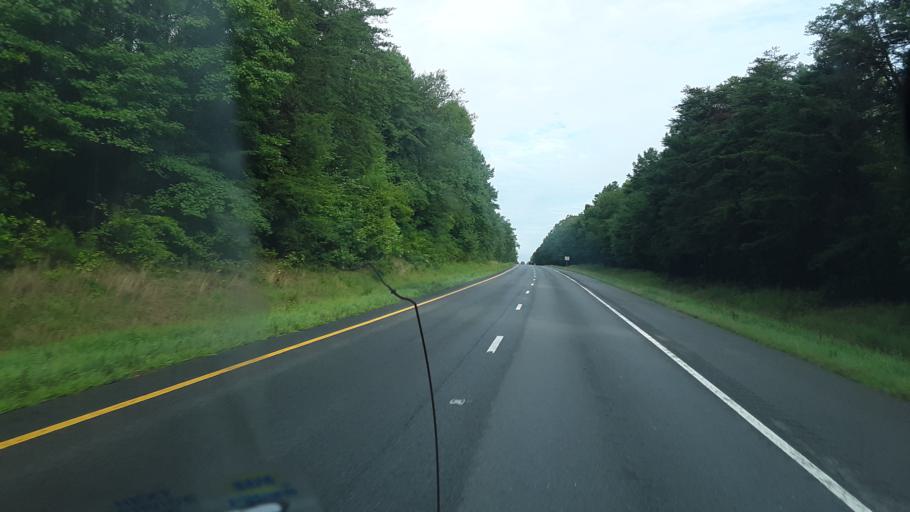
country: US
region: Virginia
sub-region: Goochland County
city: Goochland
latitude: 37.7939
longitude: -77.9039
